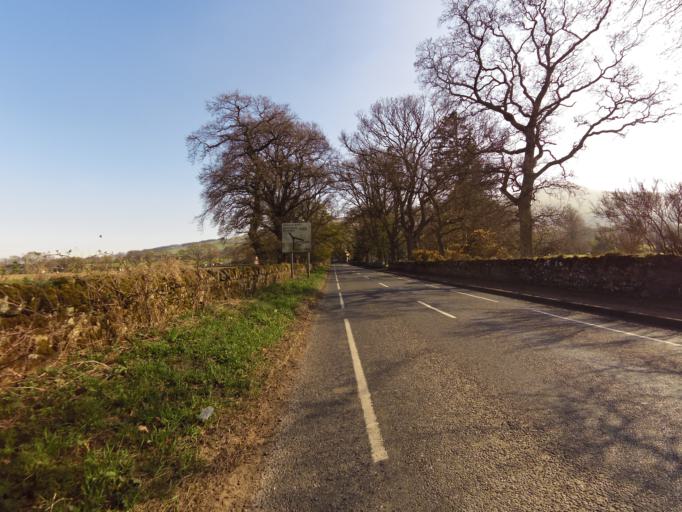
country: GB
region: Scotland
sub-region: Fife
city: Falkland
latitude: 56.2576
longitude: -3.2062
